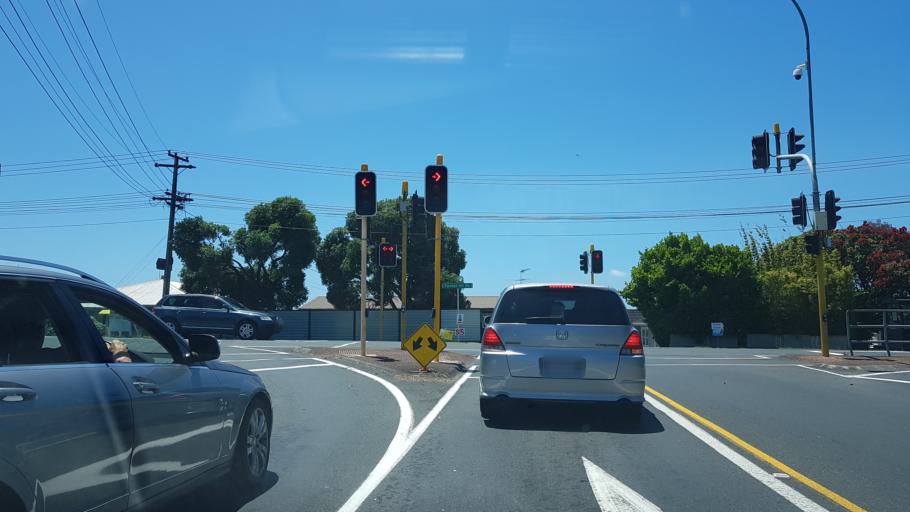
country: NZ
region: Auckland
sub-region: Auckland
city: North Shore
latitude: -36.7701
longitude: 174.7490
